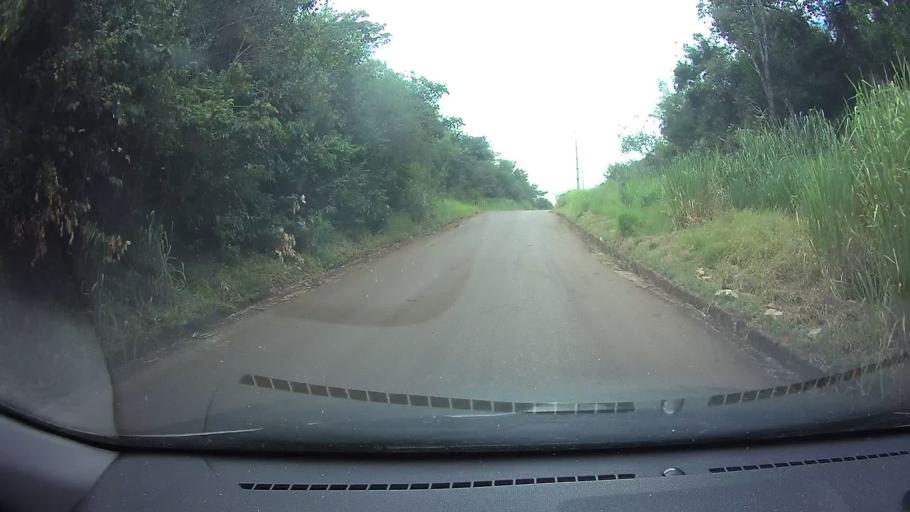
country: PY
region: Paraguari
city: La Colmena
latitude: -25.9271
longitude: -56.7902
